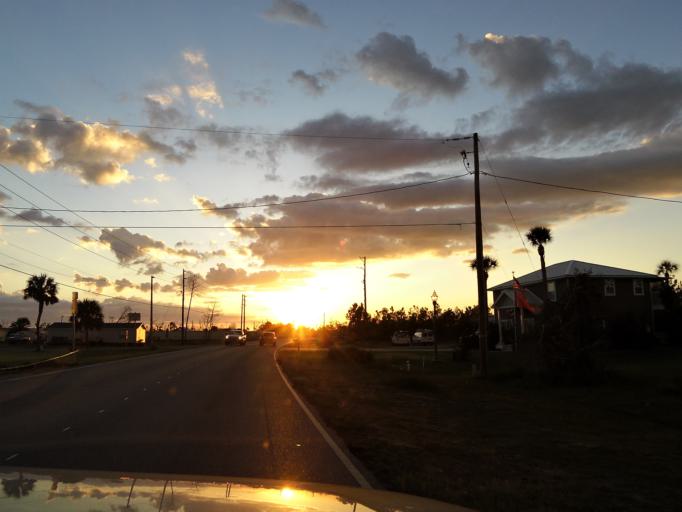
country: US
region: Florida
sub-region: Bay County
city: Mexico Beach
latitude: 29.9408
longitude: -85.3904
